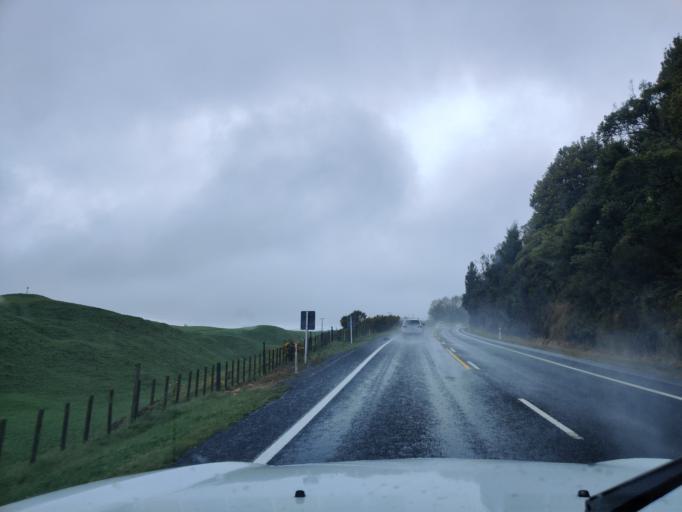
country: NZ
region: Waikato
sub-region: South Waikato District
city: Tokoroa
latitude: -38.0315
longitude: 175.9917
